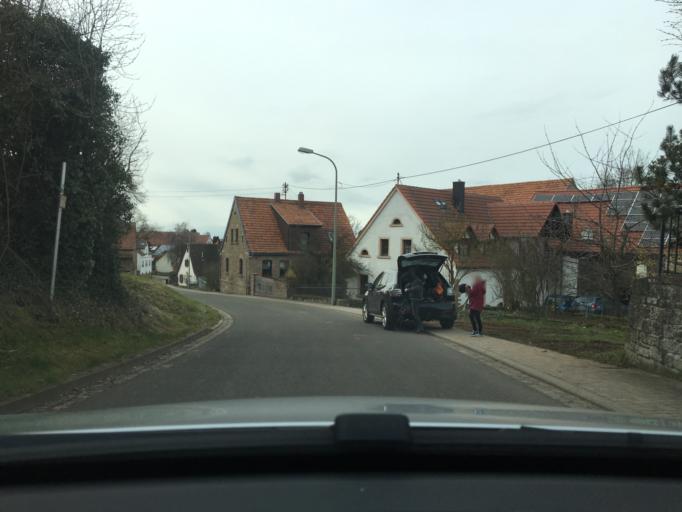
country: DE
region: Rheinland-Pfalz
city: Schonborn
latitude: 49.6415
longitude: 7.7768
